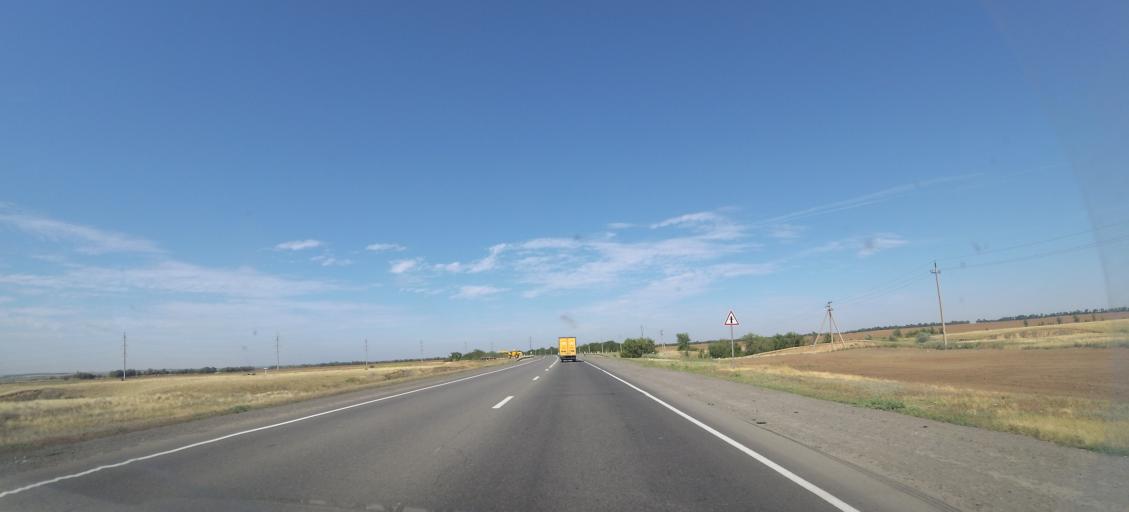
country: RU
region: Volgograd
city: Oktyabr'skiy
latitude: 48.6988
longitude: 43.8112
